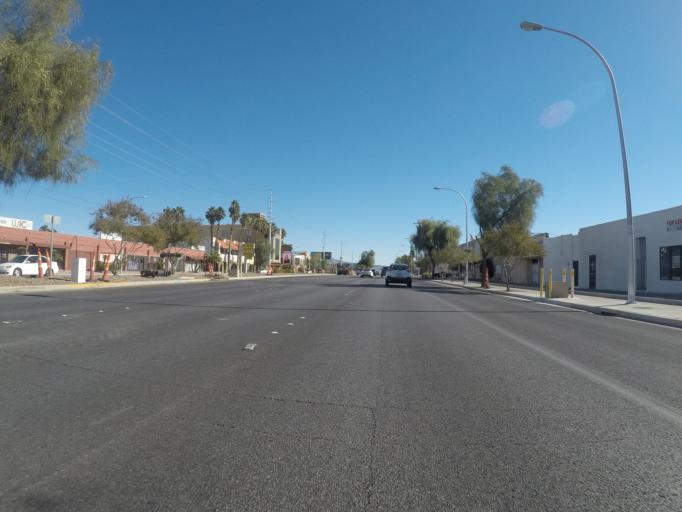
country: US
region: Nevada
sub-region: Clark County
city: Winchester
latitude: 36.1440
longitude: -115.1415
